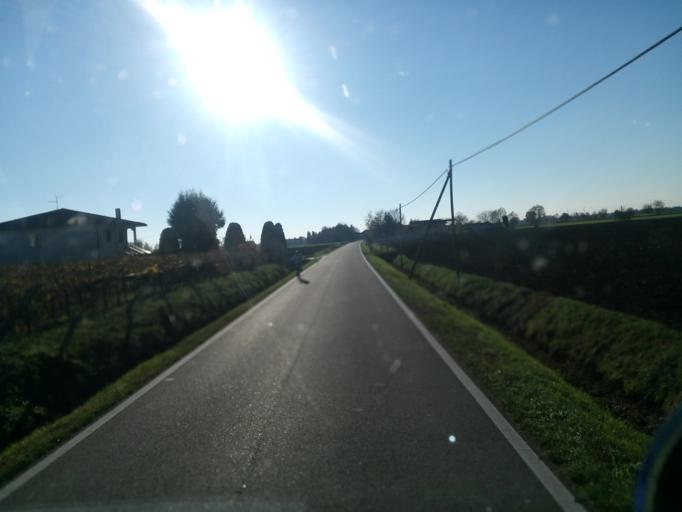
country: IT
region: Veneto
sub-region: Provincia di Vicenza
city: Asigliano Veneto
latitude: 45.3244
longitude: 11.4220
